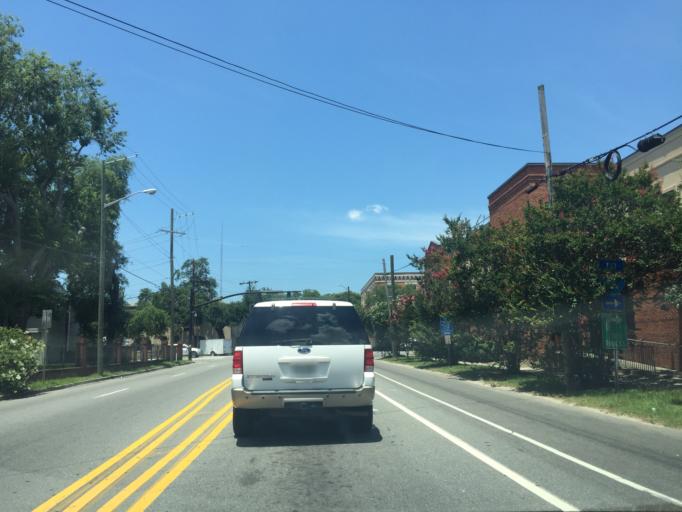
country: US
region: Georgia
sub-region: Chatham County
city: Savannah
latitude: 32.0759
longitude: -81.0843
